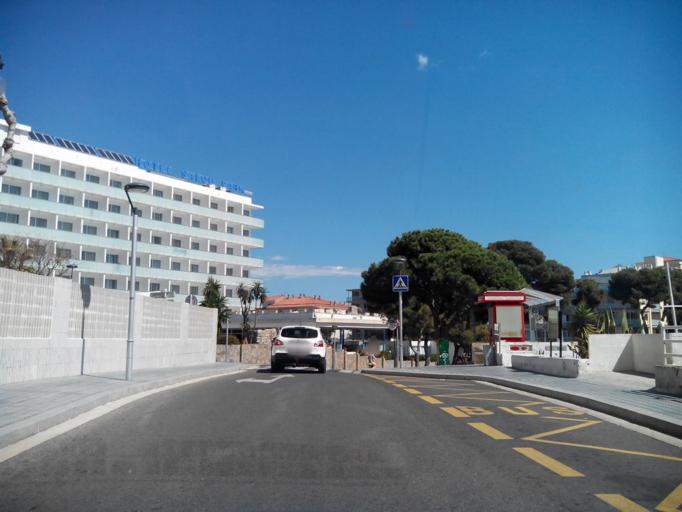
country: ES
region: Catalonia
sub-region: Provincia de Tarragona
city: Salou
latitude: 41.0695
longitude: 1.1485
